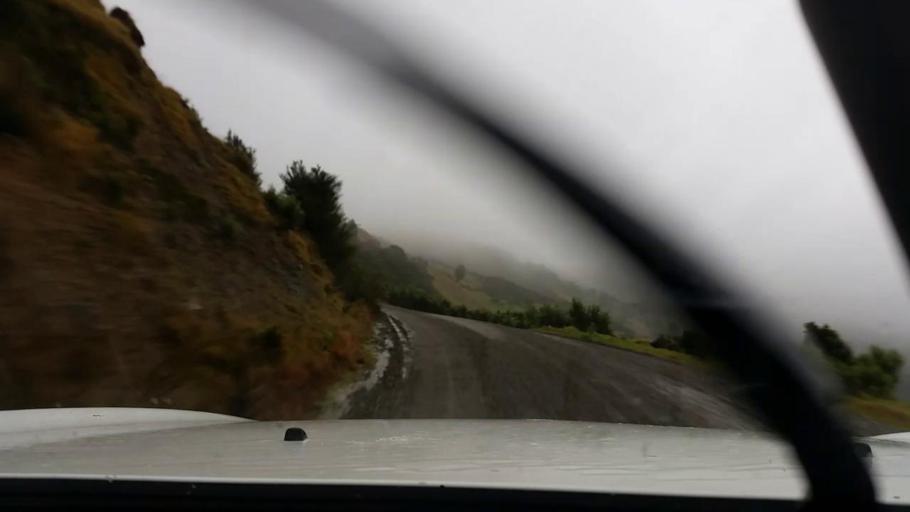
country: NZ
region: Wellington
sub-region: Masterton District
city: Masterton
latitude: -41.2495
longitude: 175.8873
